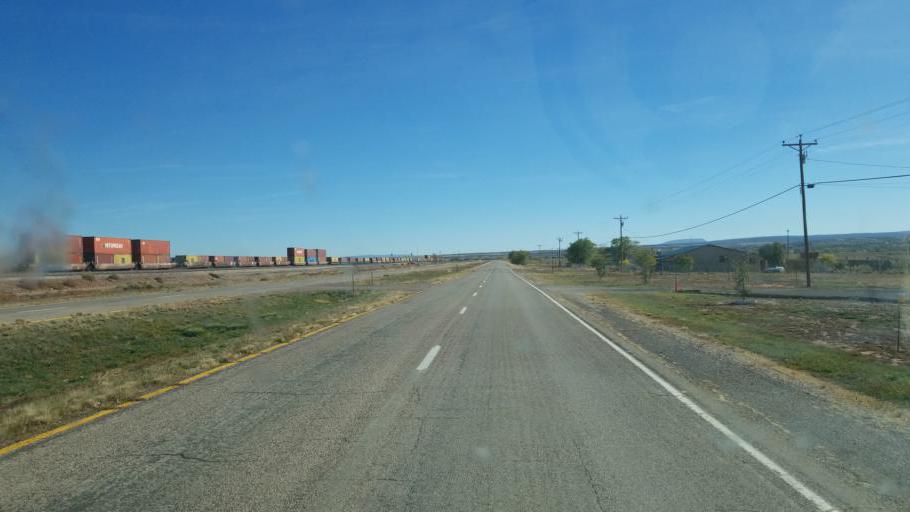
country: US
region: New Mexico
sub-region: Cibola County
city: Milan
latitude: 35.2785
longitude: -107.9823
